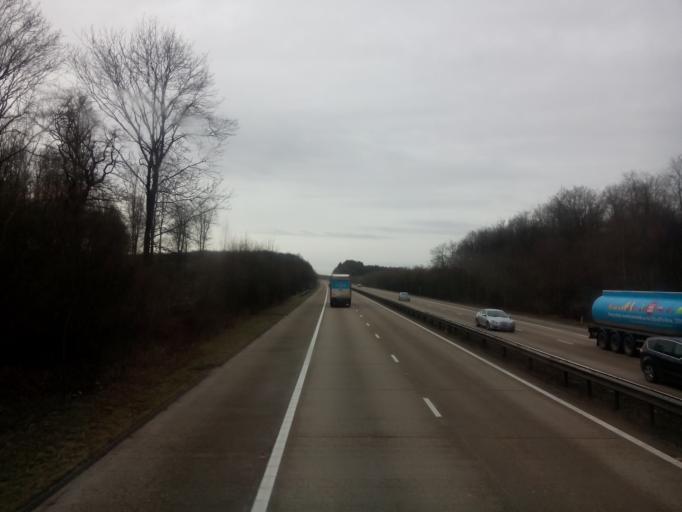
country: GB
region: England
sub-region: Hampshire
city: Kings Worthy
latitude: 51.1374
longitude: -1.2463
